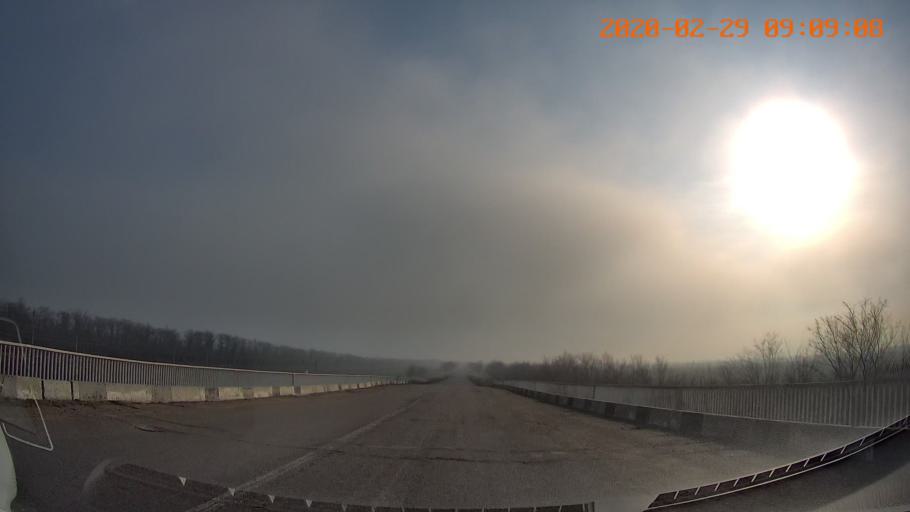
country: MD
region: Telenesti
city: Slobozia
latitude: 46.8454
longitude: 29.7578
